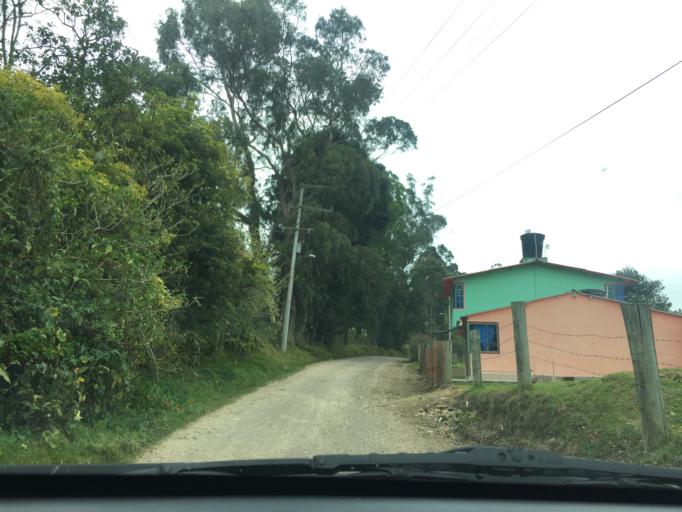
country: CO
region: Cundinamarca
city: El Rosal
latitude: 4.8836
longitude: -74.2599
